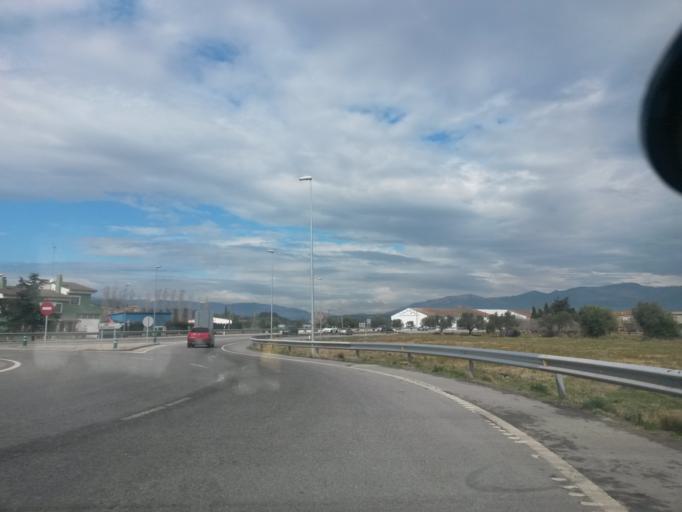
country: ES
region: Catalonia
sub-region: Provincia de Girona
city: Pont de Molins
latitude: 42.3191
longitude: 2.9317
